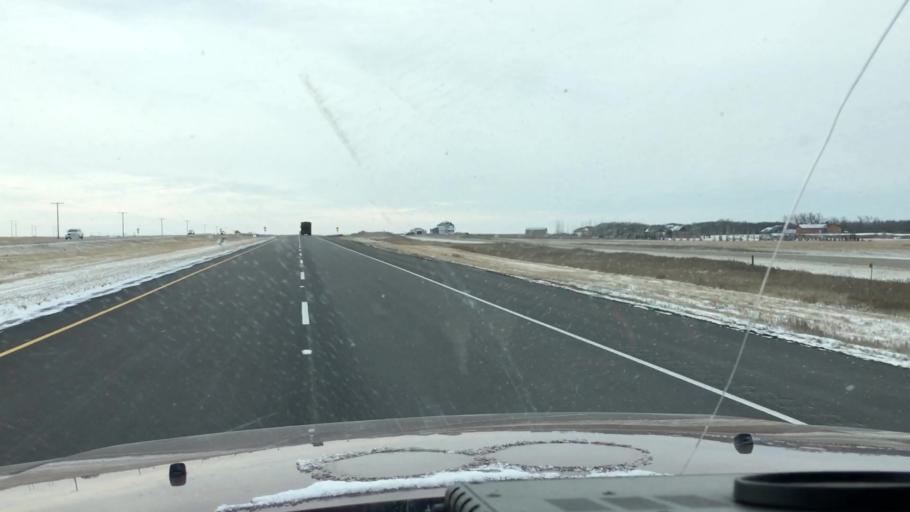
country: CA
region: Saskatchewan
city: Saskatoon
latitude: 51.9329
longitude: -106.5367
